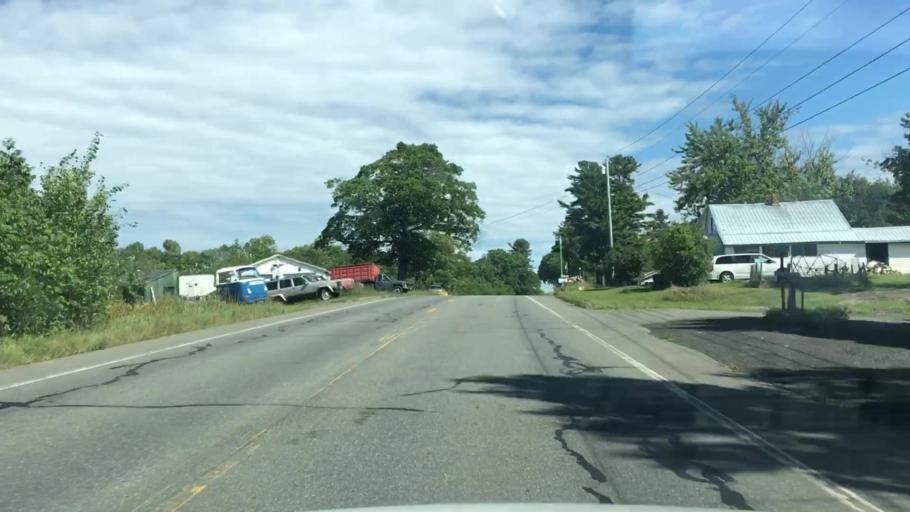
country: US
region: Maine
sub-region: Penobscot County
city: Garland
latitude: 45.0820
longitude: -69.2289
